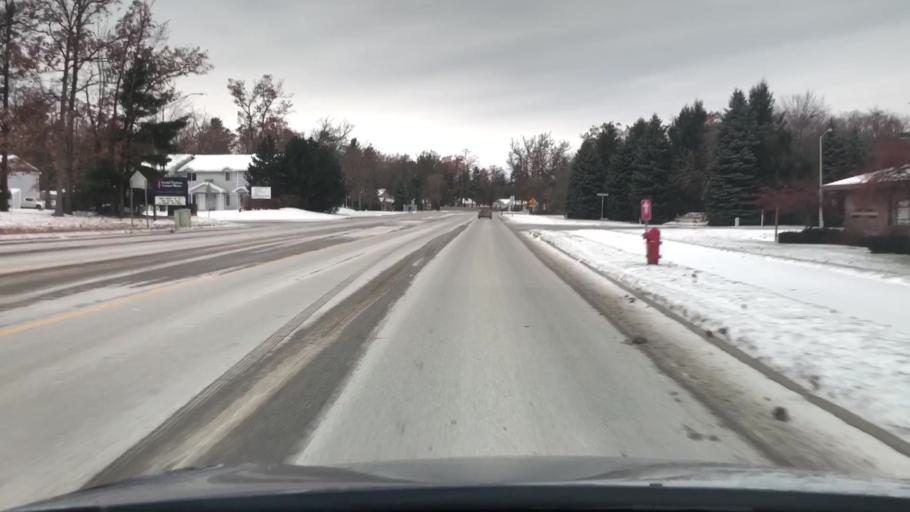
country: US
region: Michigan
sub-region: Grand Traverse County
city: Traverse City
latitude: 44.7426
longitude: -85.5604
